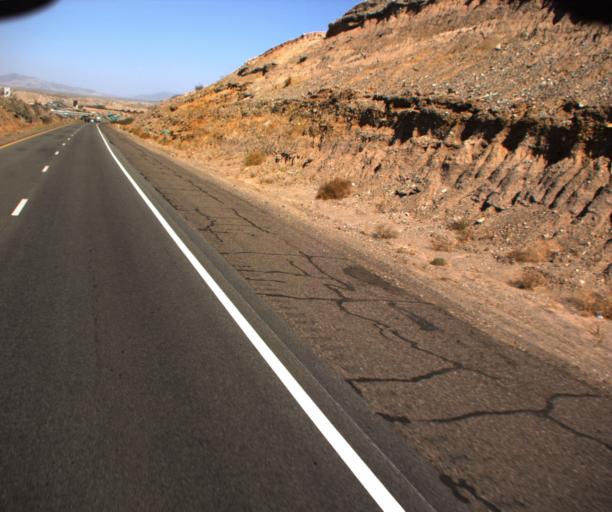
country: US
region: Arizona
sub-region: Mohave County
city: Desert Hills
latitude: 34.7185
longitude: -114.4694
